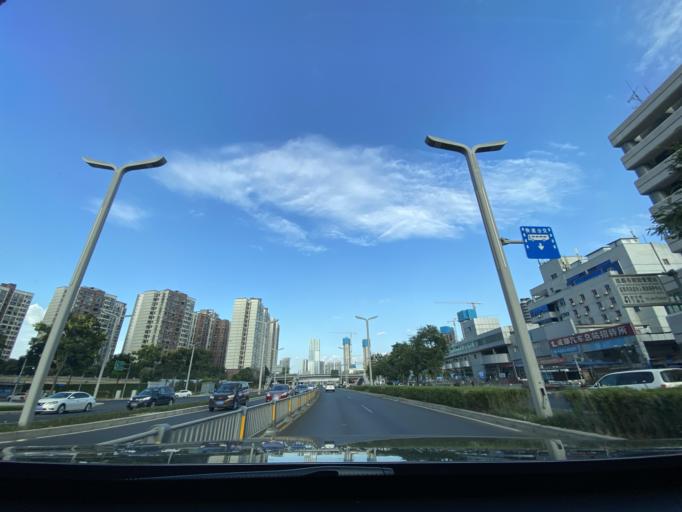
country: CN
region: Sichuan
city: Chengdu
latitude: 30.6386
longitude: 104.1245
